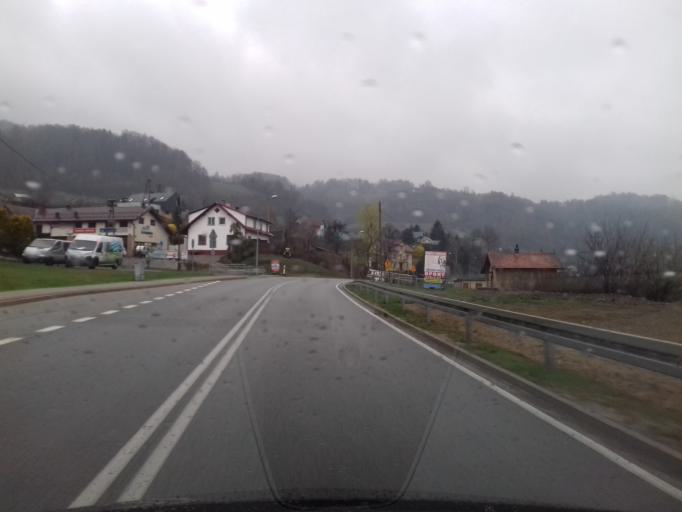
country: PL
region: Lesser Poland Voivodeship
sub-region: Powiat nowosadecki
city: Piwniczna-Zdroj
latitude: 49.4505
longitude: 20.6997
